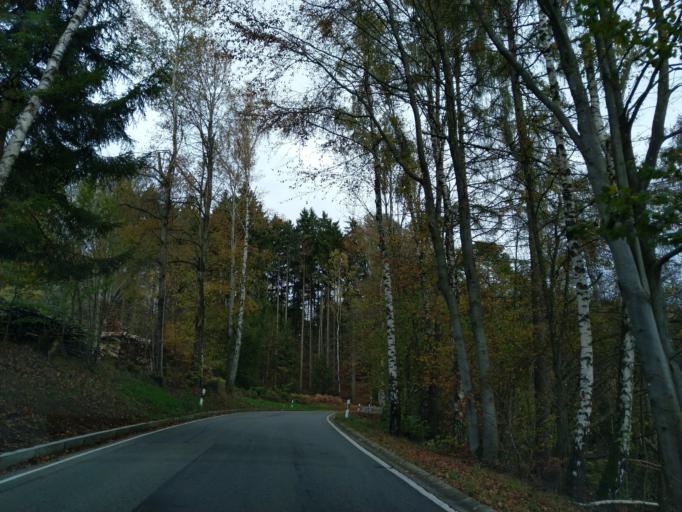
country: DE
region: Bavaria
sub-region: Lower Bavaria
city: Zenting
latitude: 48.7971
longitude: 13.2367
